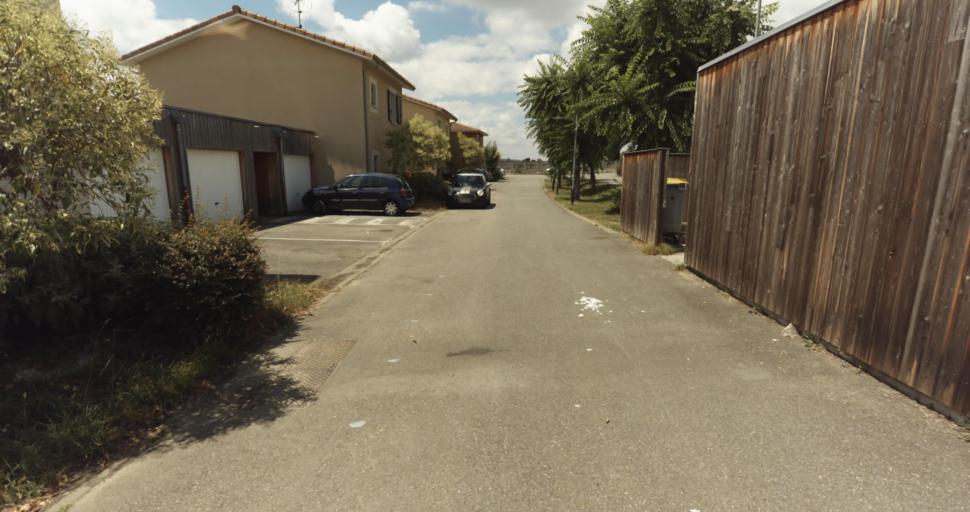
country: FR
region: Midi-Pyrenees
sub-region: Departement de la Haute-Garonne
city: Fontenilles
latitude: 43.5515
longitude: 1.1878
